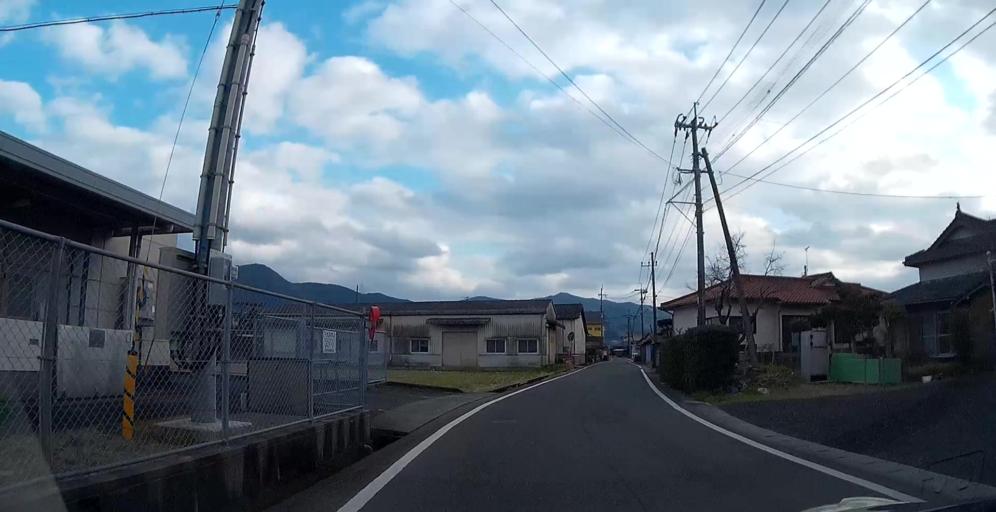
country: JP
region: Kumamoto
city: Yatsushiro
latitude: 32.5321
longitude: 130.6377
